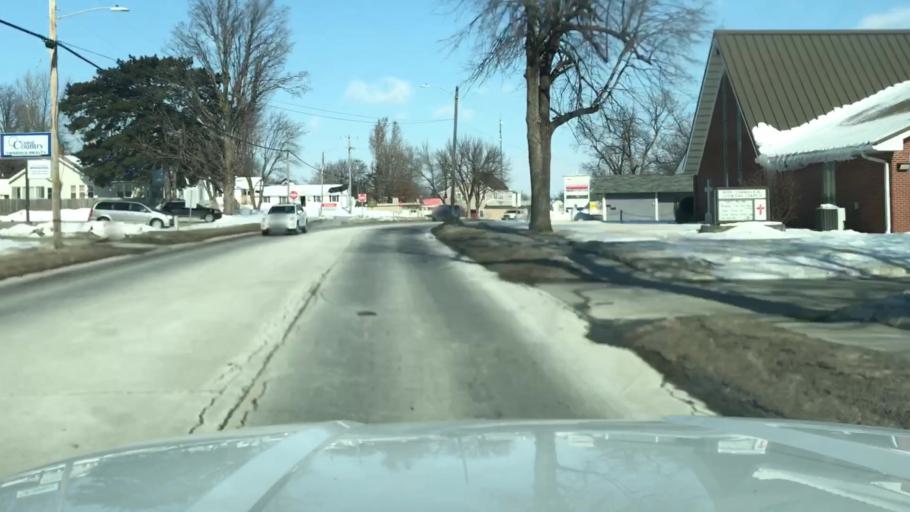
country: US
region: Missouri
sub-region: Nodaway County
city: Maryville
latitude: 40.3371
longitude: -94.8737
